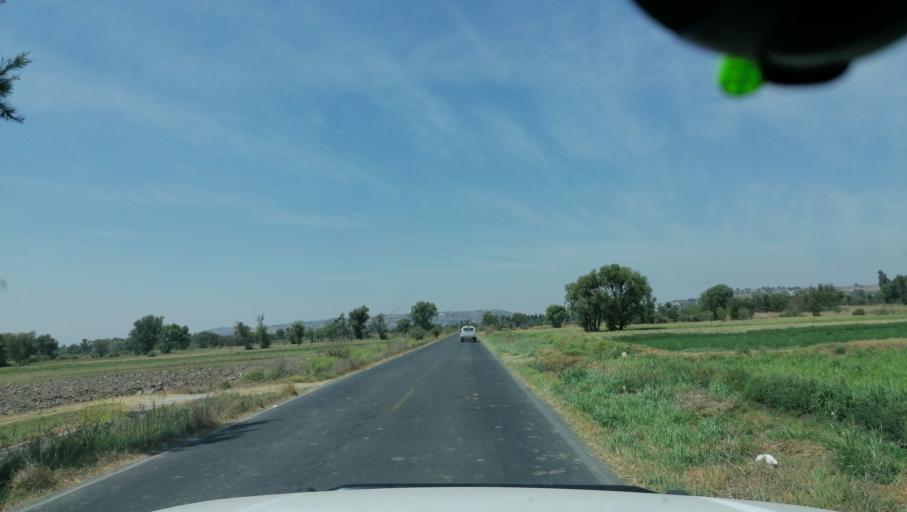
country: MX
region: Tlaxcala
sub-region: Tetlatlahuca
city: Tetlatlahuca
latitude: 19.2119
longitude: -98.2831
